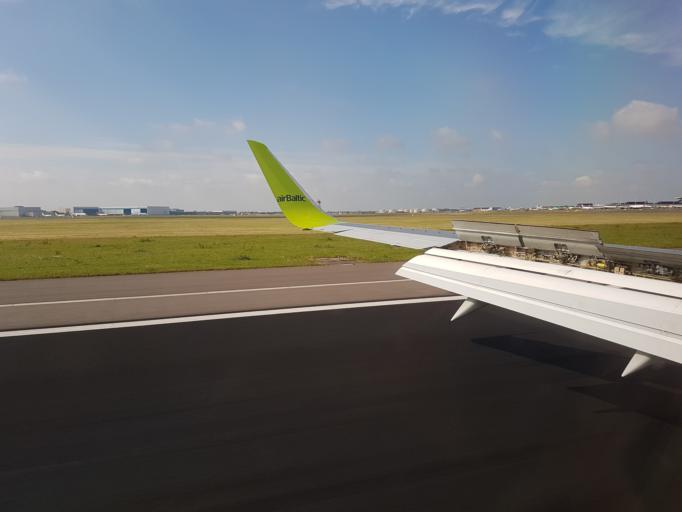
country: NL
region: North Holland
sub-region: Gemeente Aalsmeer
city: Aalsmeer
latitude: 52.3181
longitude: 4.7872
